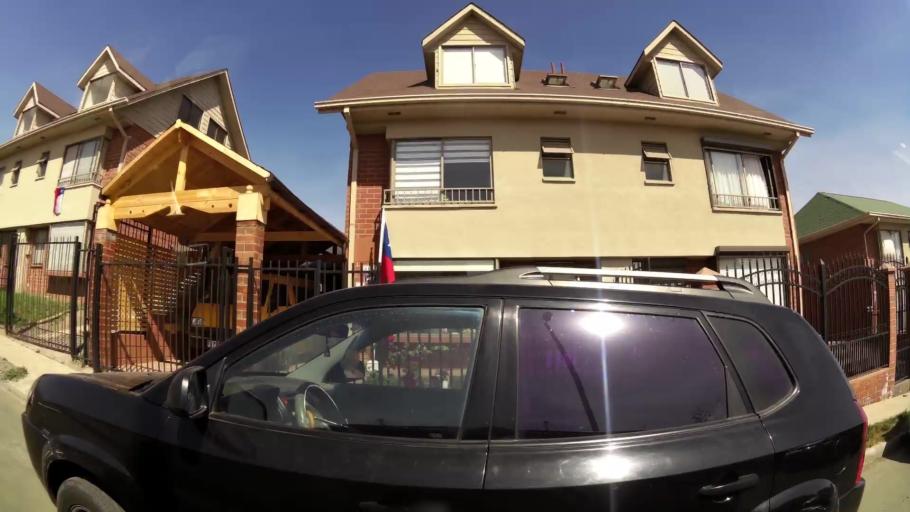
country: CL
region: Santiago Metropolitan
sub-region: Provincia de Cordillera
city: Puente Alto
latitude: -33.5405
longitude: -70.5482
